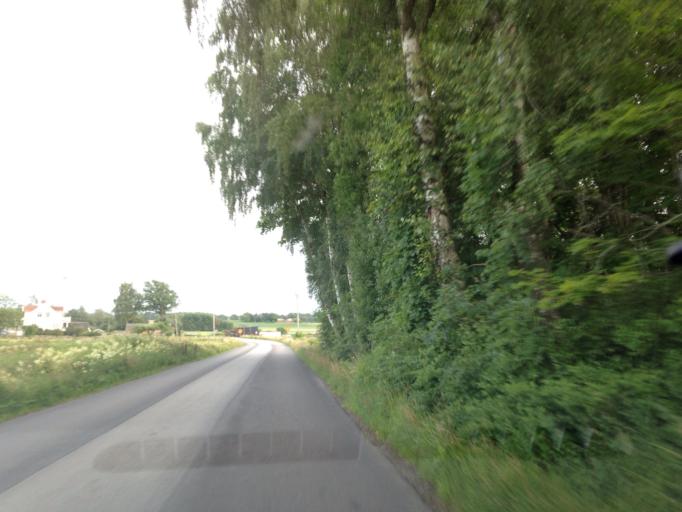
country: SE
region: Halland
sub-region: Varbergs Kommun
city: Tvaaker
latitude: 57.1288
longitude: 12.3872
